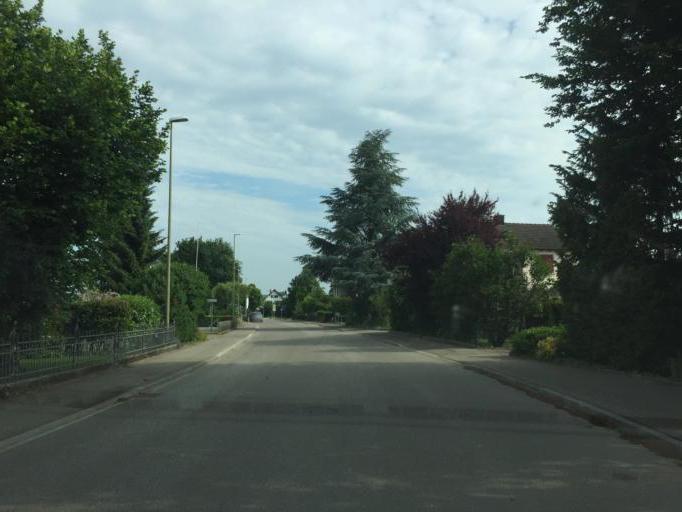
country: CH
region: Zurich
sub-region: Bezirk Andelfingen
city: Dachsen
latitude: 47.6366
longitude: 8.6006
